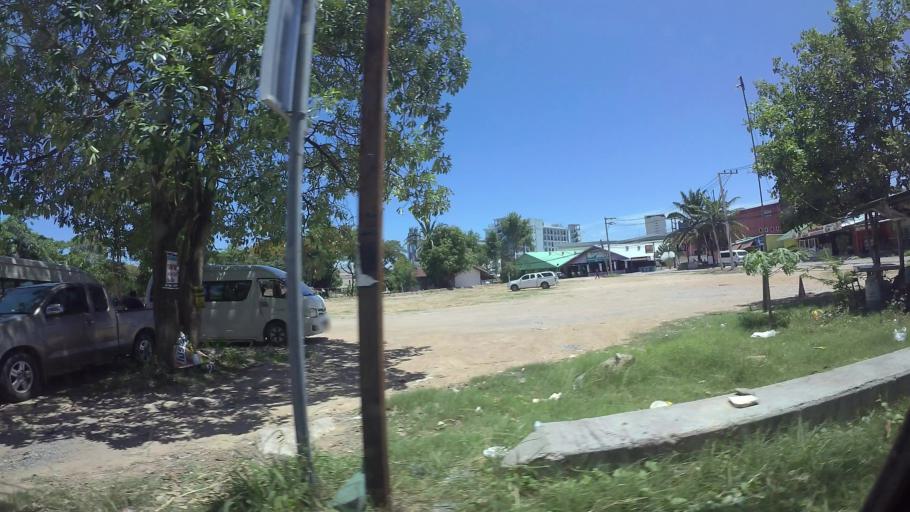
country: TH
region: Chon Buri
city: Phatthaya
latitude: 12.9439
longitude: 100.8980
